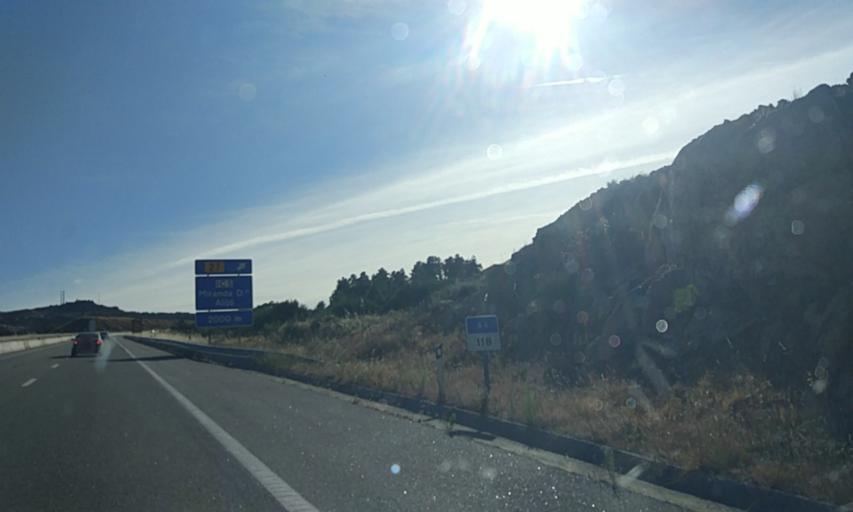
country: PT
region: Vila Real
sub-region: Murca
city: Murca
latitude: 41.3922
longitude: -7.4853
